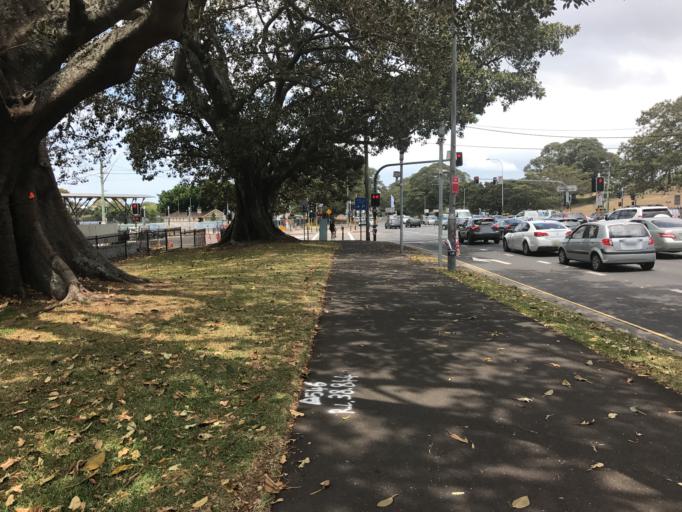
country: AU
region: New South Wales
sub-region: Woollahra
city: Paddington
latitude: -33.8947
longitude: 151.2216
